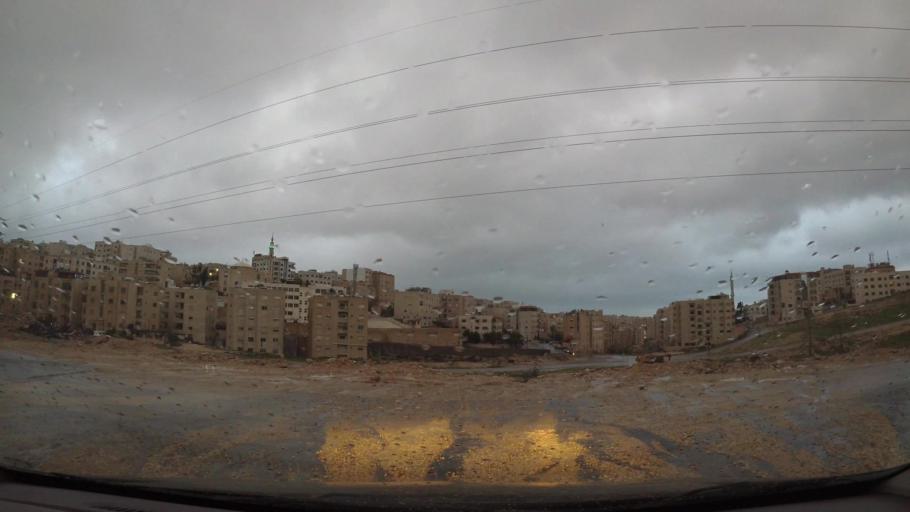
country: JO
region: Amman
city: Amman
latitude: 32.0000
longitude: 35.9292
